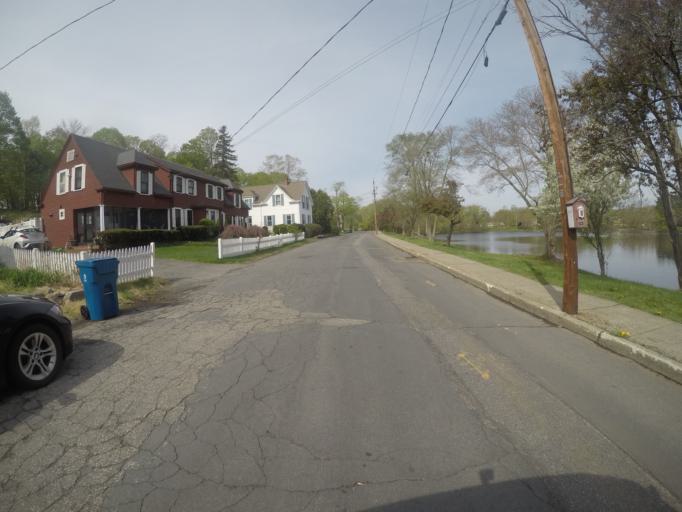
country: US
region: Massachusetts
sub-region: Bristol County
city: Easton
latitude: 42.0682
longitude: -71.0996
